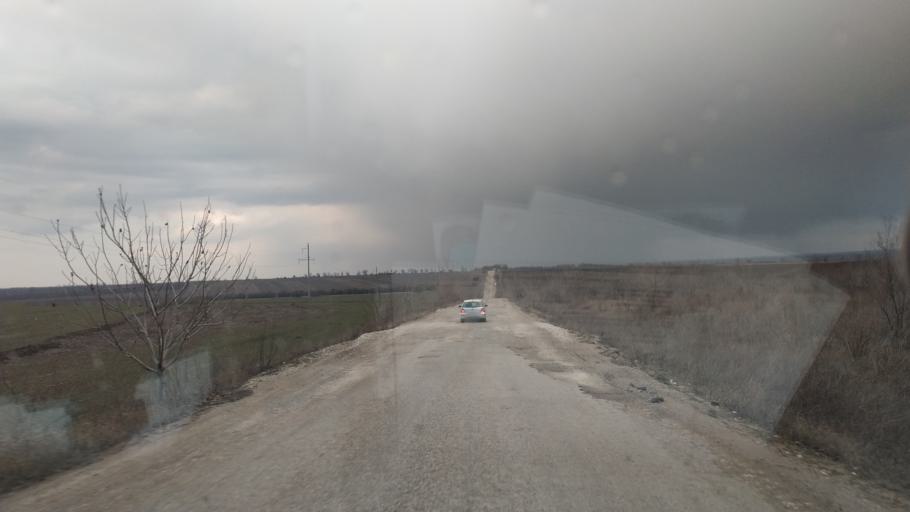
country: MD
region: Telenesti
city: Grigoriopol
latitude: 47.0575
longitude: 29.2954
